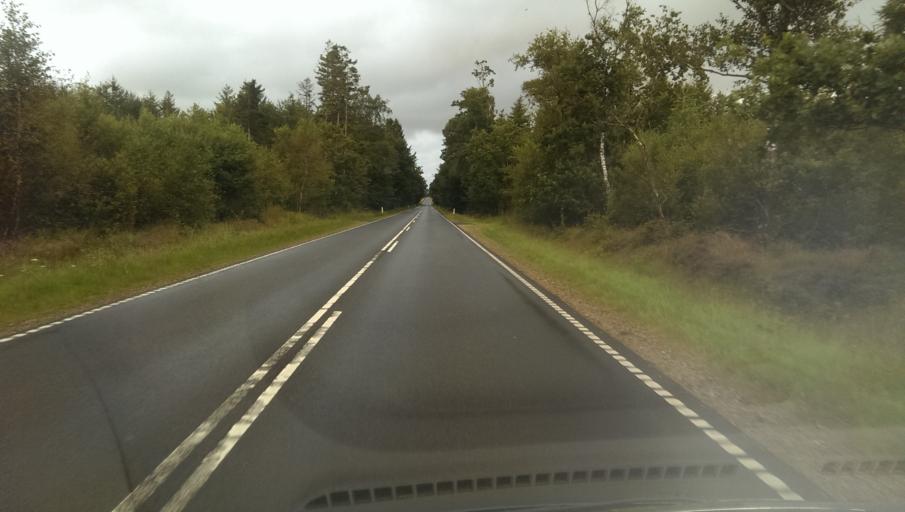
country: DK
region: South Denmark
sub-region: Varde Kommune
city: Olgod
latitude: 55.6948
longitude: 8.6056
